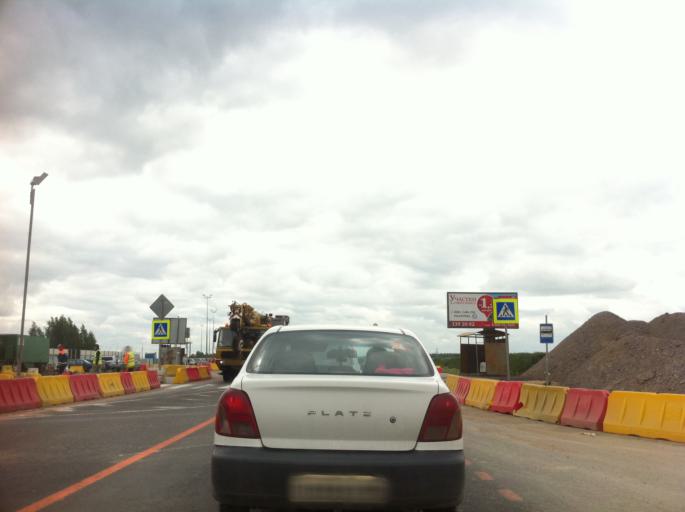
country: RU
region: Leningrad
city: Maloye Verevo
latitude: 59.6707
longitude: 30.2322
